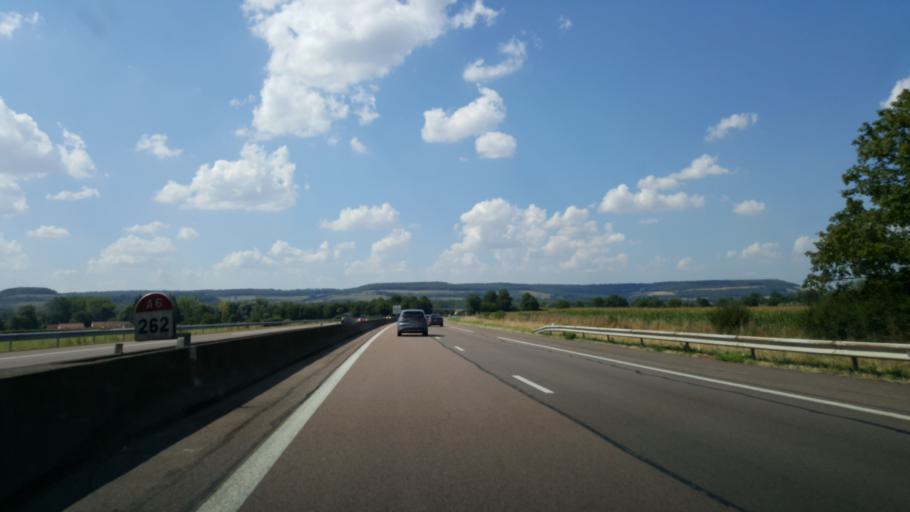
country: FR
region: Bourgogne
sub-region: Departement de la Cote-d'Or
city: Pouilly-en-Auxois
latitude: 47.2591
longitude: 4.5270
